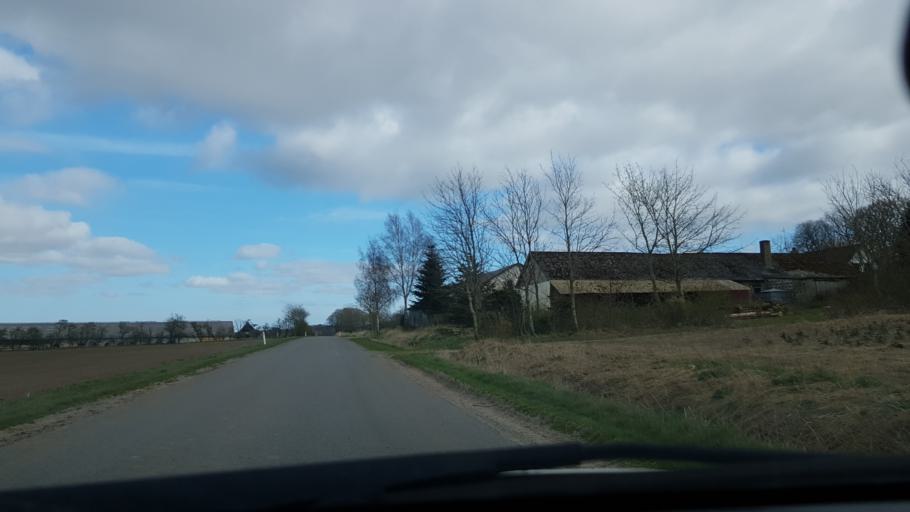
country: DK
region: South Denmark
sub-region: Vejen Kommune
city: Brorup
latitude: 55.4301
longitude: 9.0472
